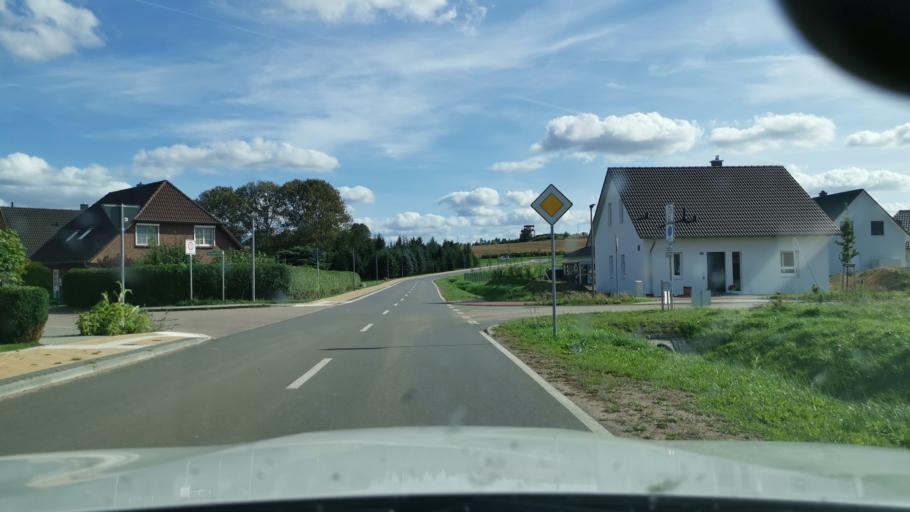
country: DE
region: Mecklenburg-Vorpommern
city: Tessin
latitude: 54.0274
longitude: 12.4506
